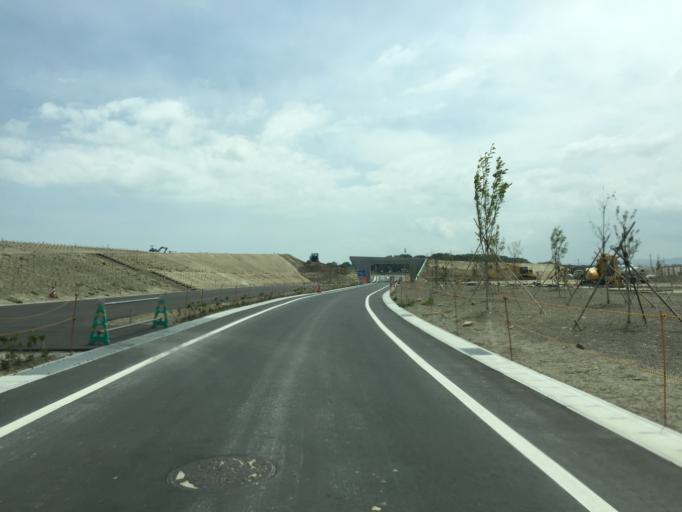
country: JP
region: Miyagi
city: Marumori
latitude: 37.8783
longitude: 140.9326
